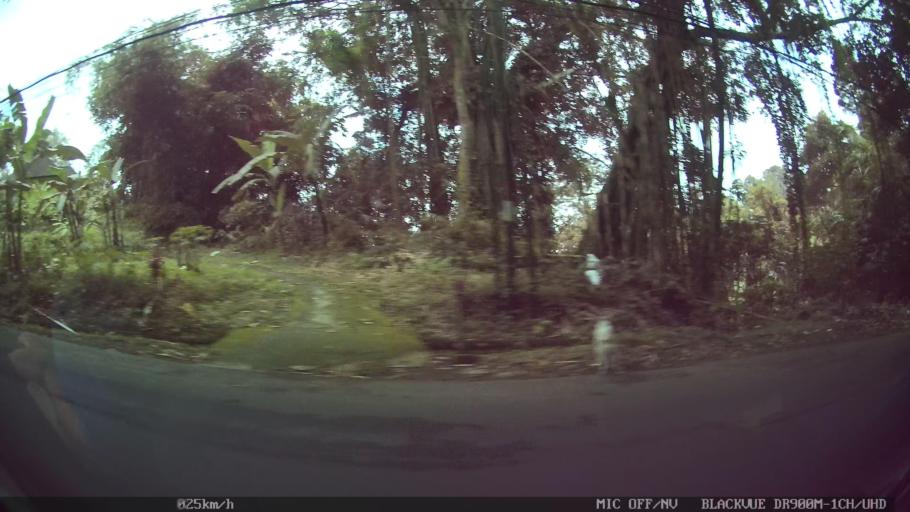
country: ID
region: Bali
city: Banjar Brahmanabukit
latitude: -8.4456
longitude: 115.3760
